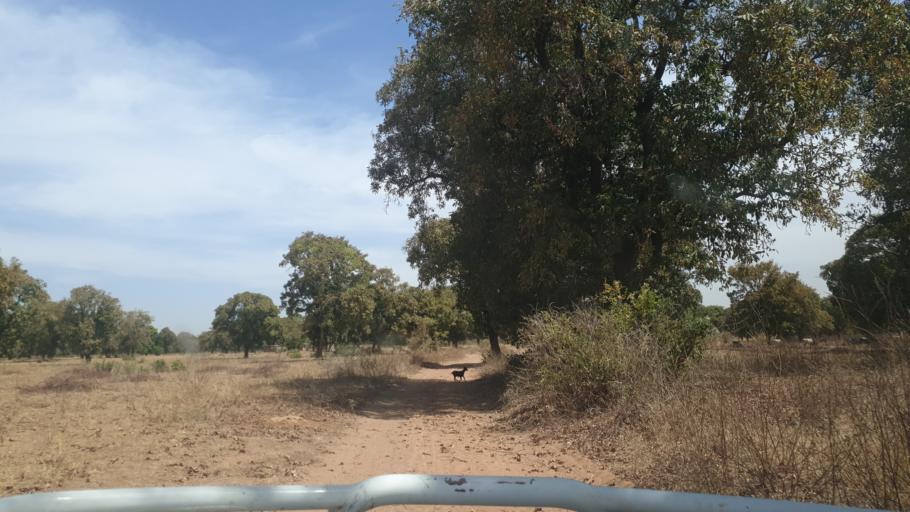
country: ML
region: Sikasso
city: Yorosso
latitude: 12.2898
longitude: -4.6697
